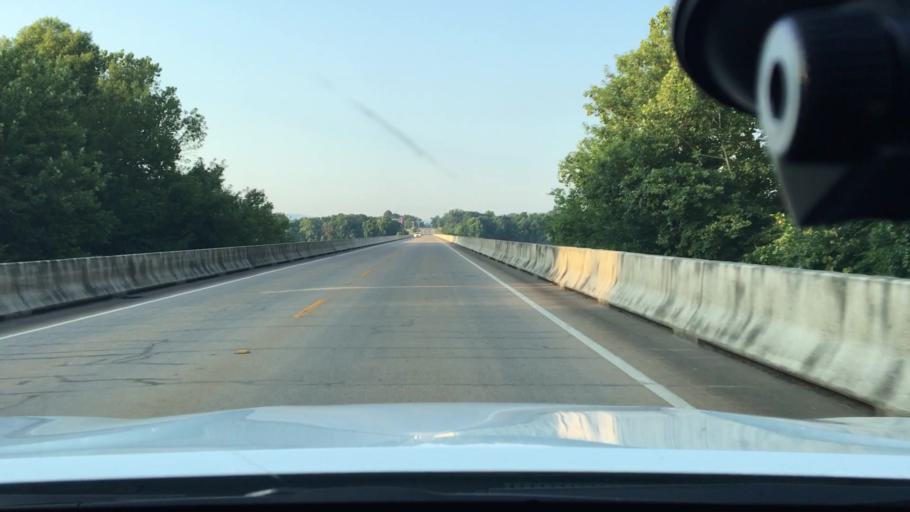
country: US
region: Arkansas
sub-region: Johnson County
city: Clarksville
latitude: 35.3970
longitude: -93.5308
